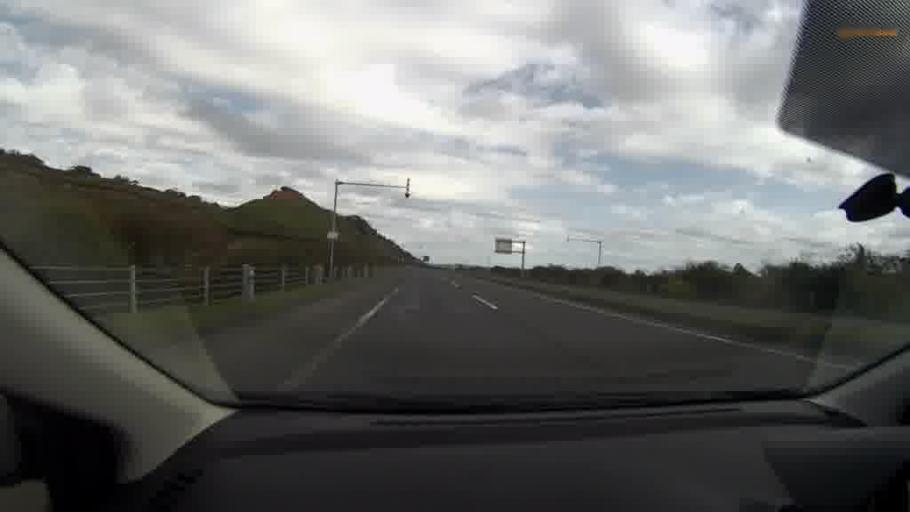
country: JP
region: Hokkaido
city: Kushiro
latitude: 43.0139
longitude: 144.2565
